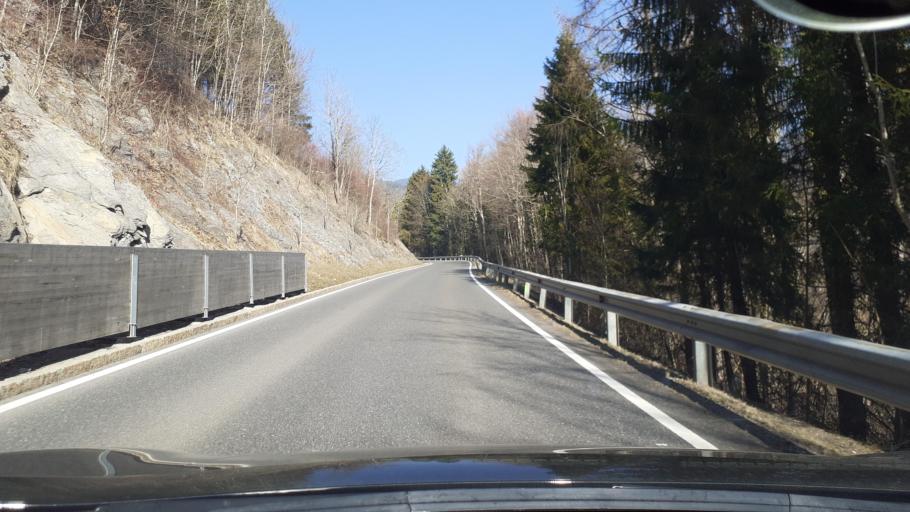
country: AT
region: Vorarlberg
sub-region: Politischer Bezirk Feldkirch
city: Fraxern
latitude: 47.3111
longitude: 9.6715
